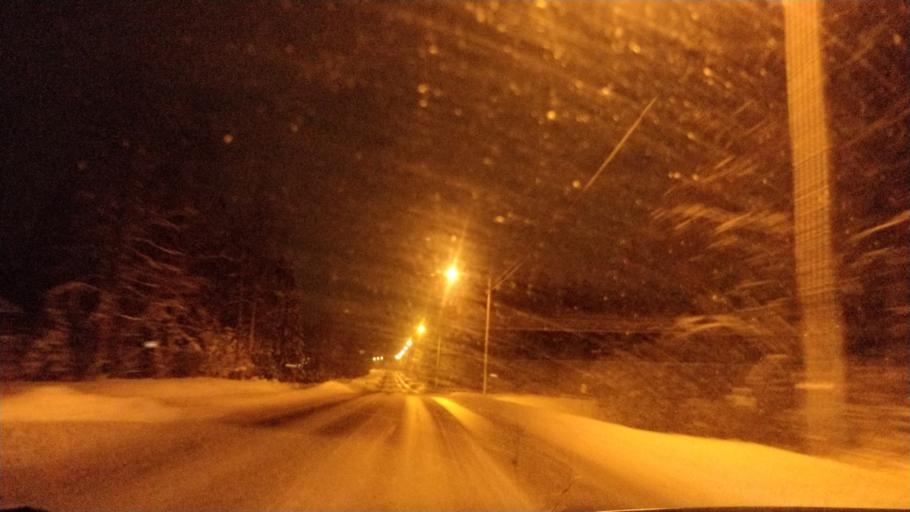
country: FI
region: Lapland
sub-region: Rovaniemi
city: Rovaniemi
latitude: 66.3844
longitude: 25.3772
